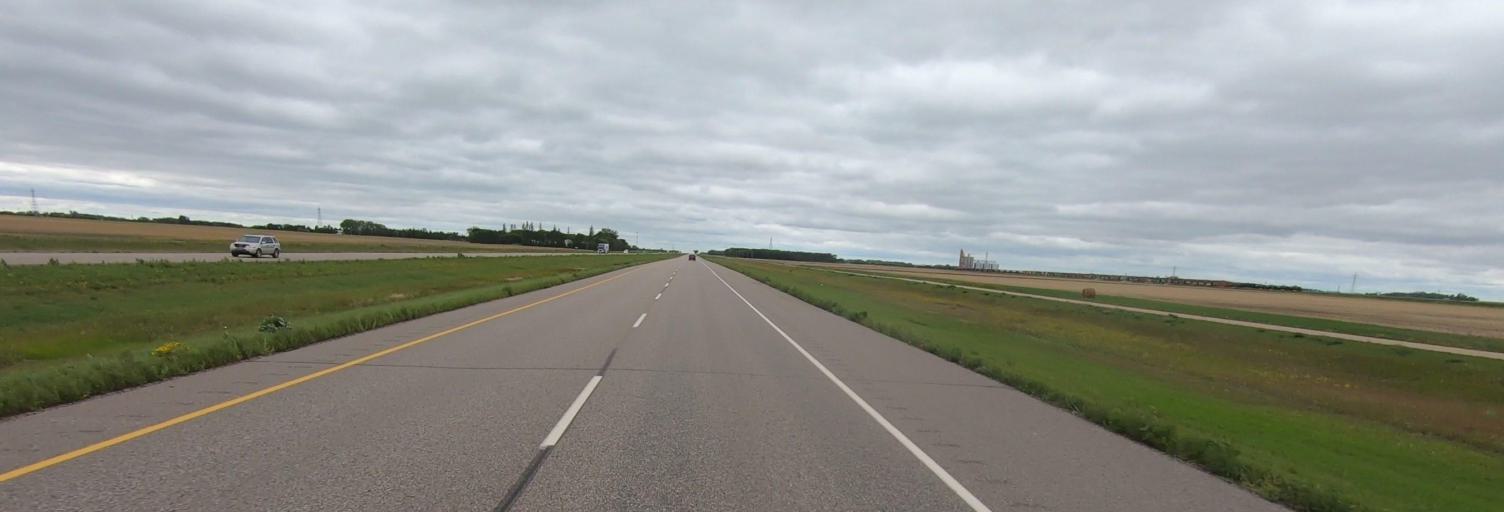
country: CA
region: Manitoba
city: Portage la Prairie
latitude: 49.9752
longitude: -98.5245
